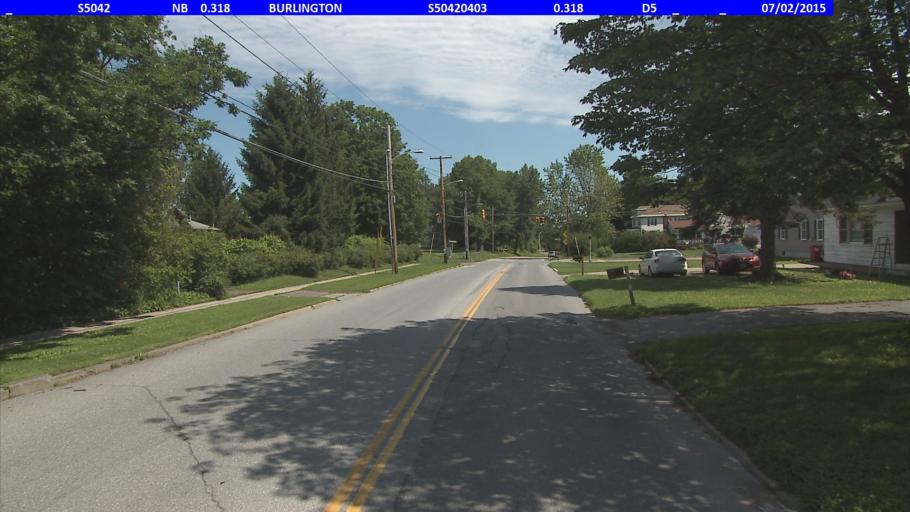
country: US
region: Vermont
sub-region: Chittenden County
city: Burlington
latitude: 44.5204
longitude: -73.2573
